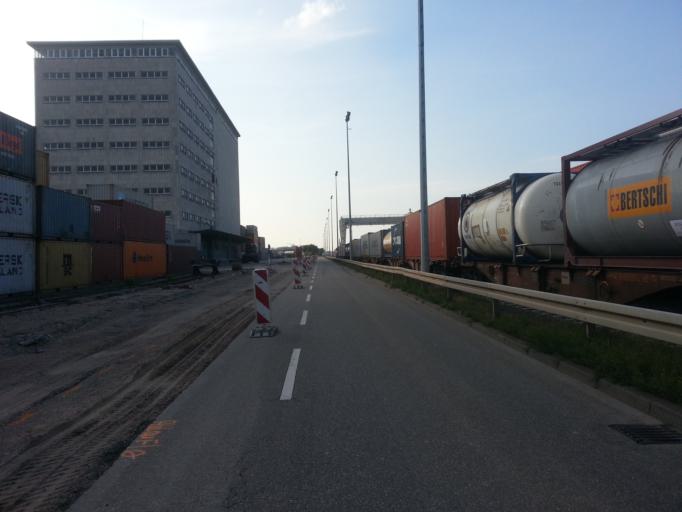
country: DE
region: Rheinland-Pfalz
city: Ludwigshafen am Rhein
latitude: 49.5010
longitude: 8.4454
